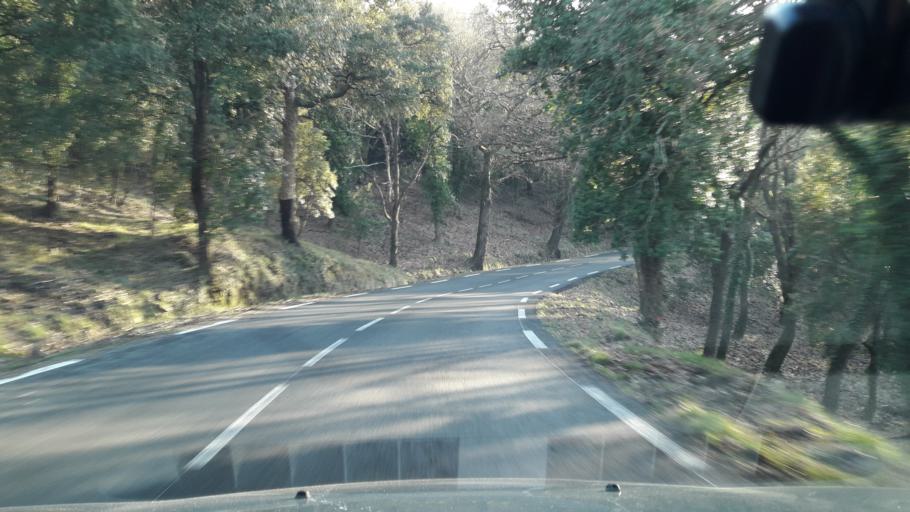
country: FR
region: Provence-Alpes-Cote d'Azur
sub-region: Departement du Var
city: Tanneron
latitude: 43.5152
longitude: 6.8177
